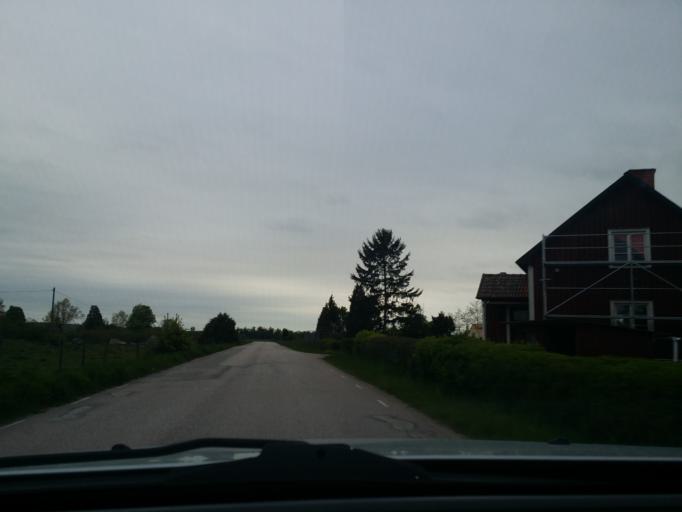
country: SE
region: Vaestmanland
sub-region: Hallstahammars Kommun
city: Kolback
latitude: 59.5442
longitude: 16.3098
